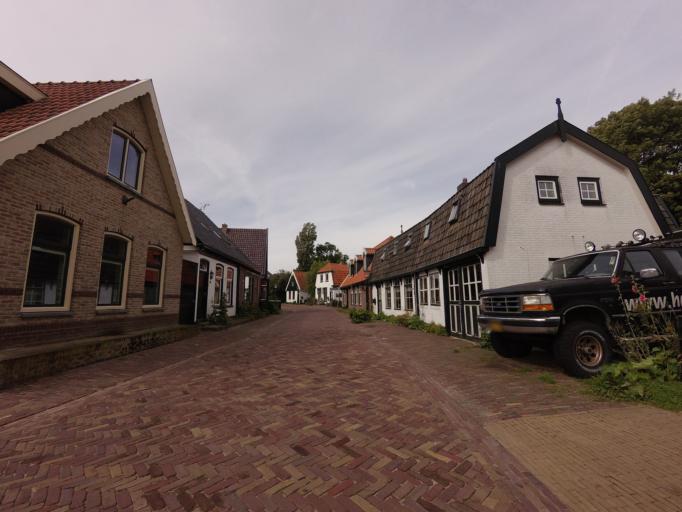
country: NL
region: North Holland
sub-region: Gemeente Texel
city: Den Burg
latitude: 53.0725
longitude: 4.8243
